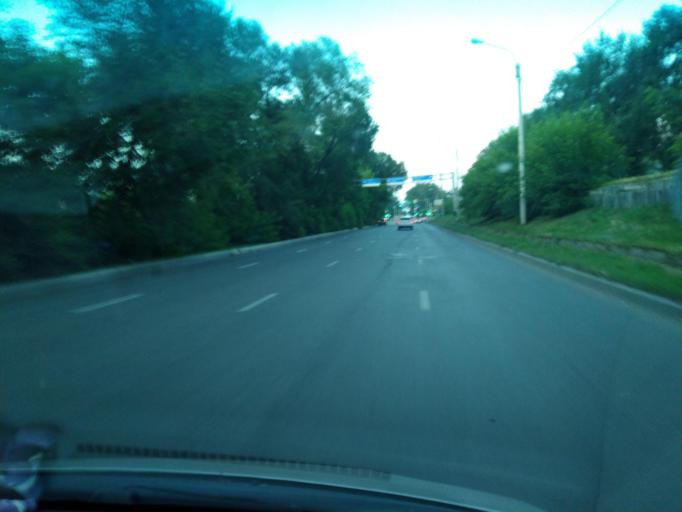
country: RU
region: Krasnoyarskiy
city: Krasnoyarsk
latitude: 55.9844
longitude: 92.8839
